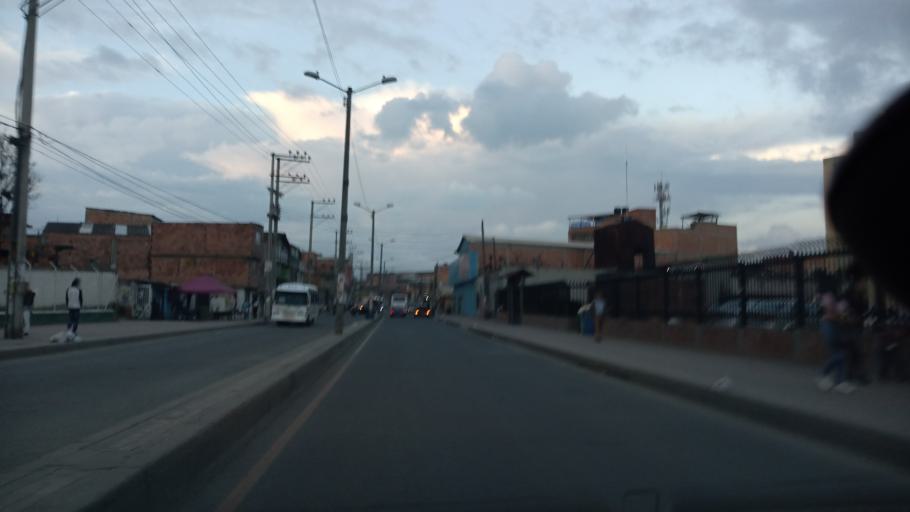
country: CO
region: Cundinamarca
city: Soacha
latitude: 4.5787
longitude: -74.2223
